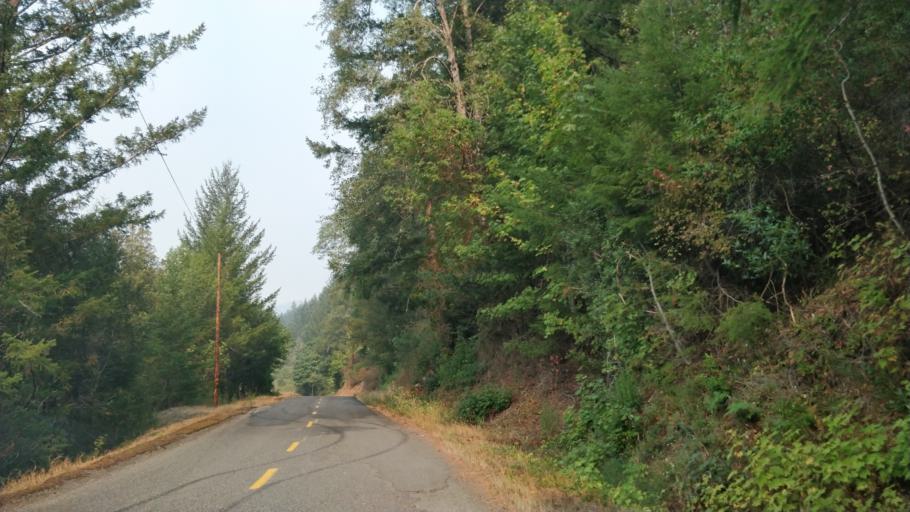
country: US
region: California
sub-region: Humboldt County
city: Rio Dell
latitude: 40.2319
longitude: -124.1393
